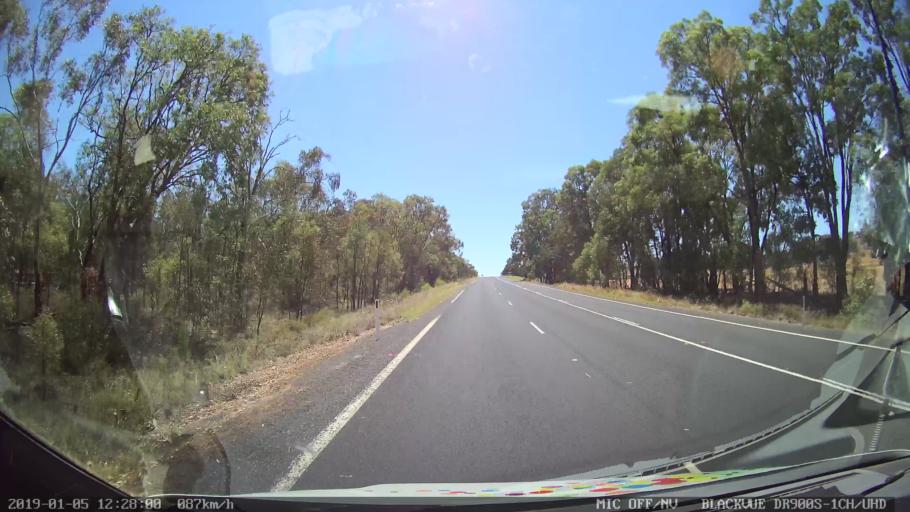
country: AU
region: New South Wales
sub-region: Warrumbungle Shire
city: Coonabarabran
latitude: -31.2435
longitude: 149.3170
